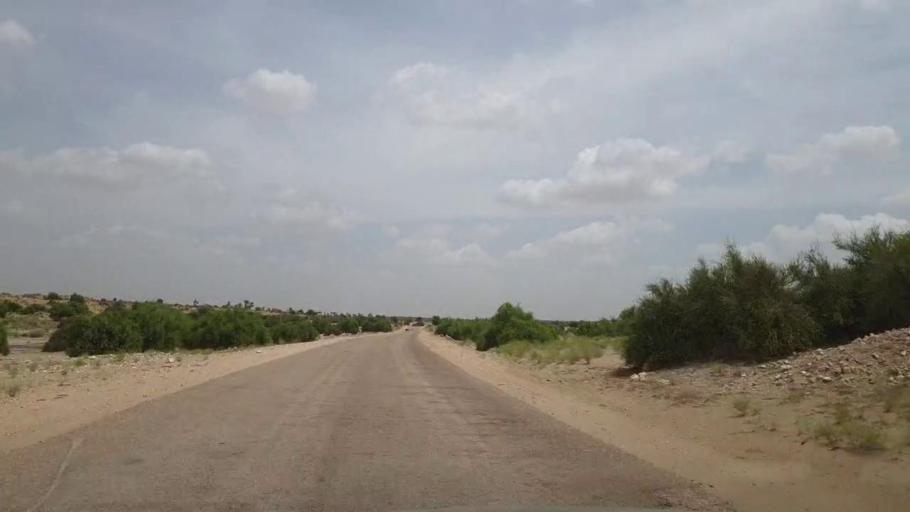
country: PK
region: Sindh
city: Kot Diji
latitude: 27.1907
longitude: 69.1677
